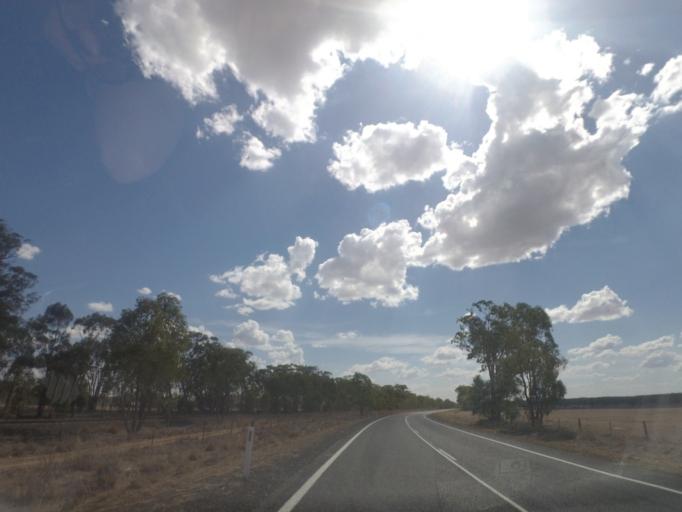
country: AU
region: Queensland
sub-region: Southern Downs
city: Stanthorpe
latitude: -28.3939
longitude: 151.3142
